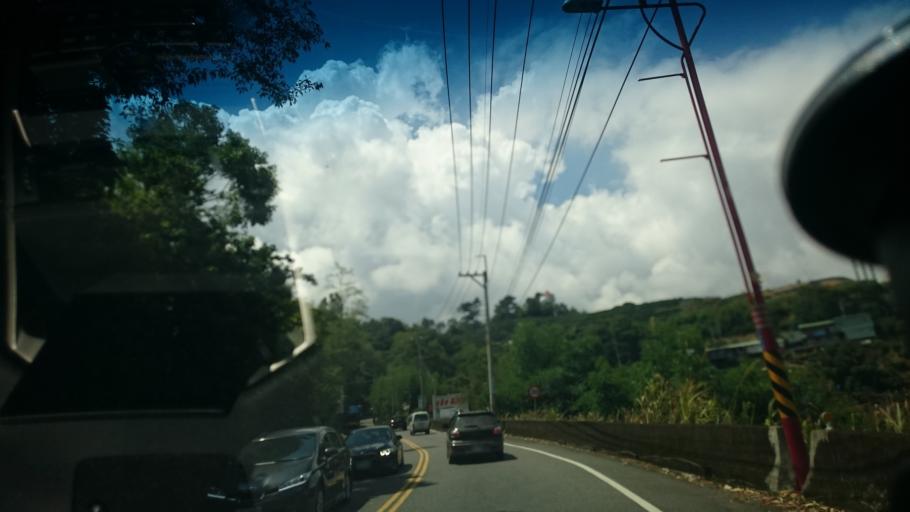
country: TW
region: Taiwan
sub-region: Nantou
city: Puli
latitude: 24.0268
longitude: 121.1444
